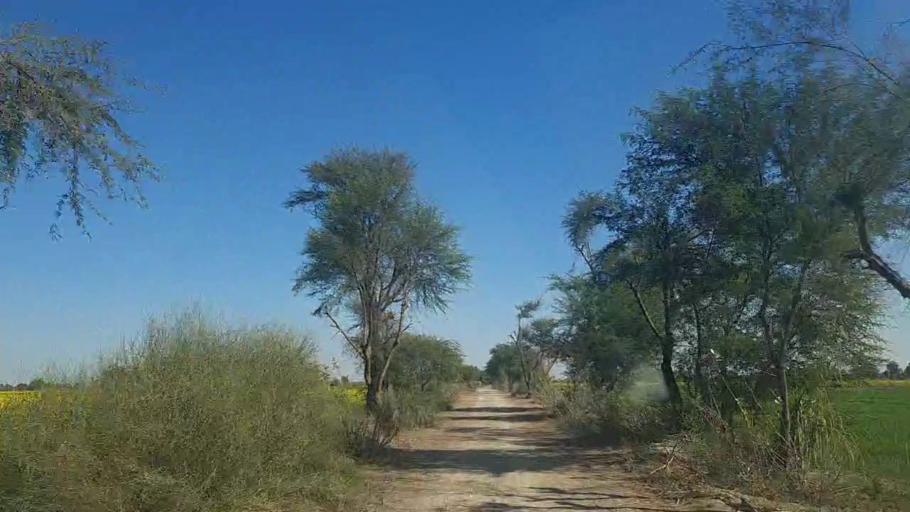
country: PK
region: Sindh
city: Khadro
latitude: 26.2180
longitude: 68.8642
